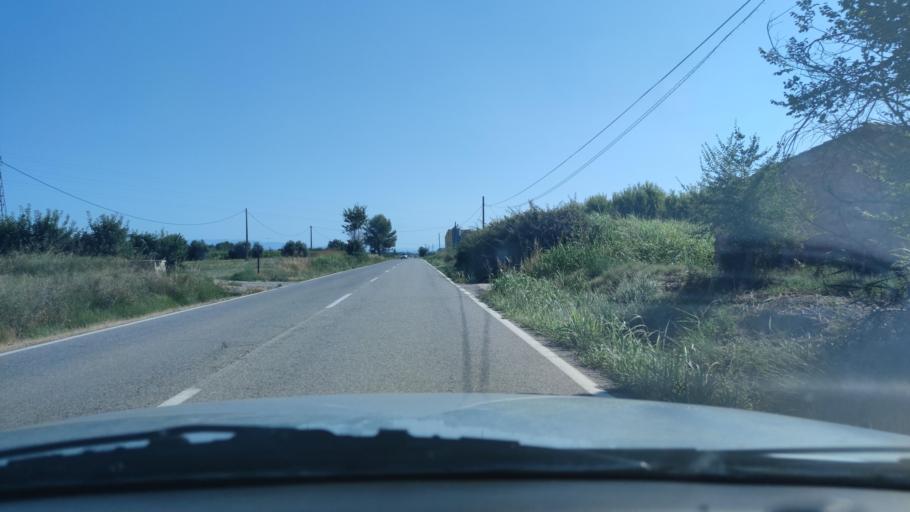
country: ES
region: Catalonia
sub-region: Provincia de Lleida
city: Bellvis
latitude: 41.6493
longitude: 0.8002
